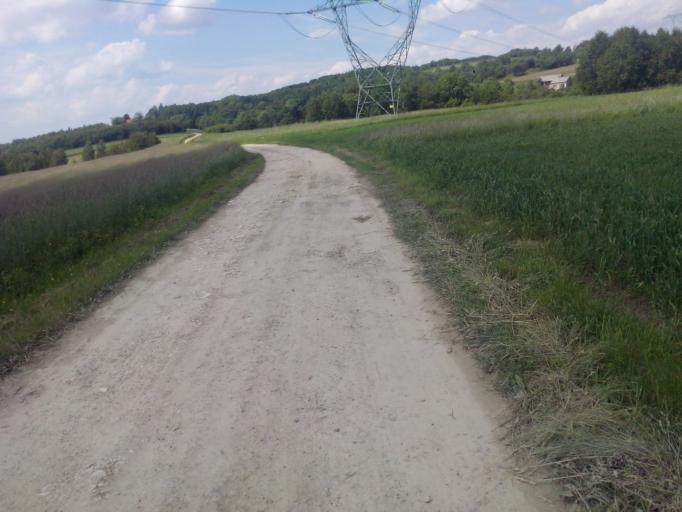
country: PL
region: Subcarpathian Voivodeship
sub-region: Powiat strzyzowski
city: Jawornik
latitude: 49.8437
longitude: 21.8526
